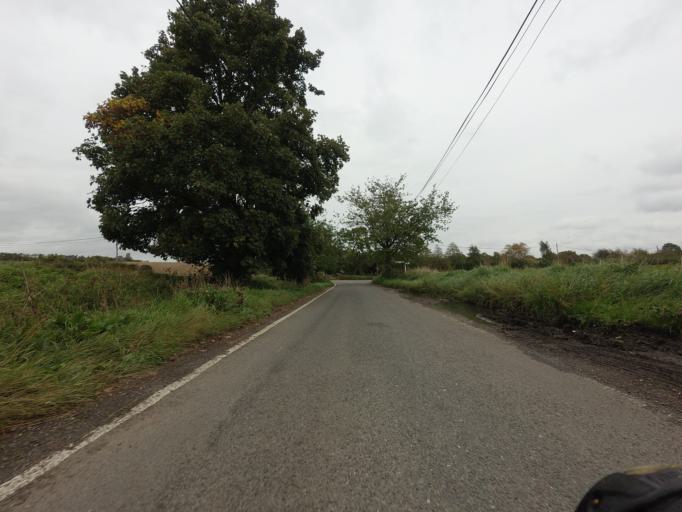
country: GB
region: England
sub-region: Cambridgeshire
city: Duxford
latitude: 52.0197
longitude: 0.1261
